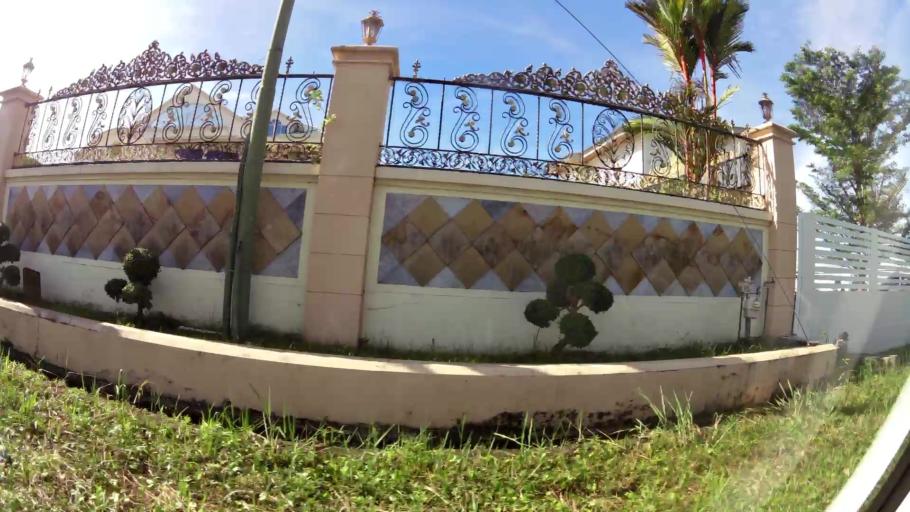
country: BN
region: Belait
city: Kuala Belait
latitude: 4.5857
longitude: 114.2144
